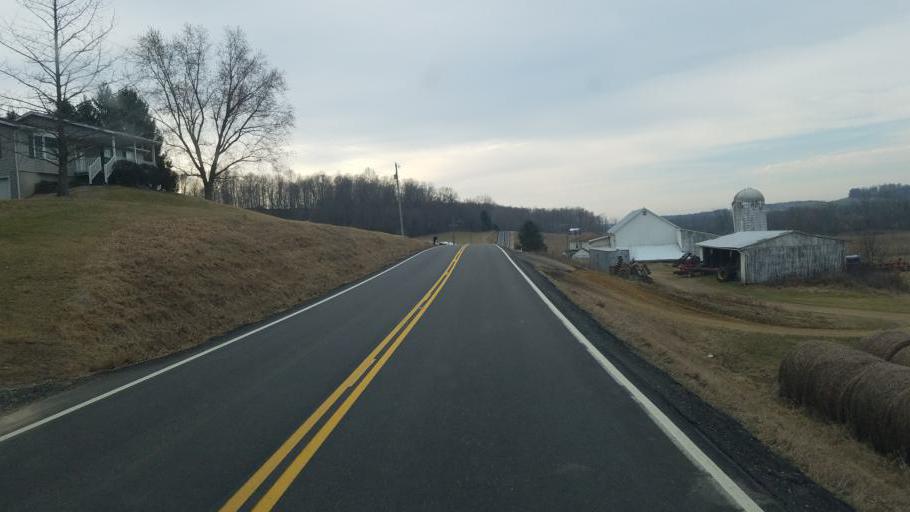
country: US
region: Ohio
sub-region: Knox County
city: Danville
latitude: 40.5193
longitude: -82.2978
